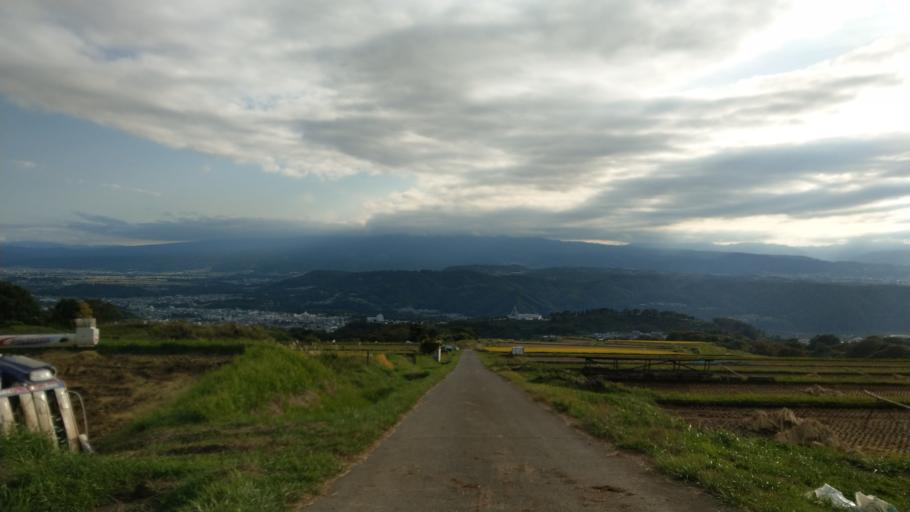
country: JP
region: Nagano
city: Komoro
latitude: 36.3569
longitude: 138.4287
